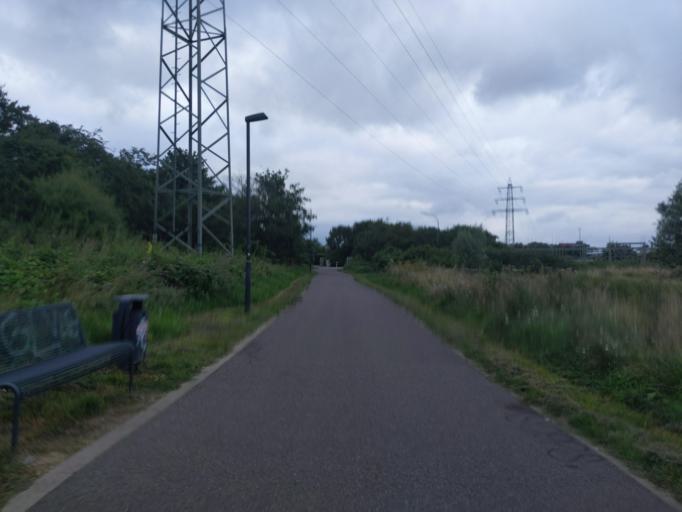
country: DE
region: North Rhine-Westphalia
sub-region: Regierungsbezirk Dusseldorf
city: Meerbusch
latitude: 51.2434
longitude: 6.7078
